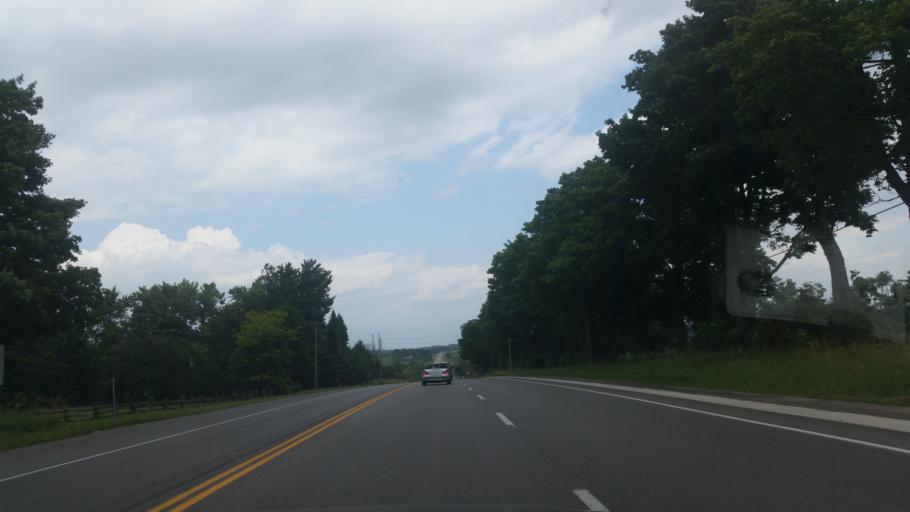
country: CA
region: Ontario
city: Orangeville
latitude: 43.7128
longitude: -80.1179
